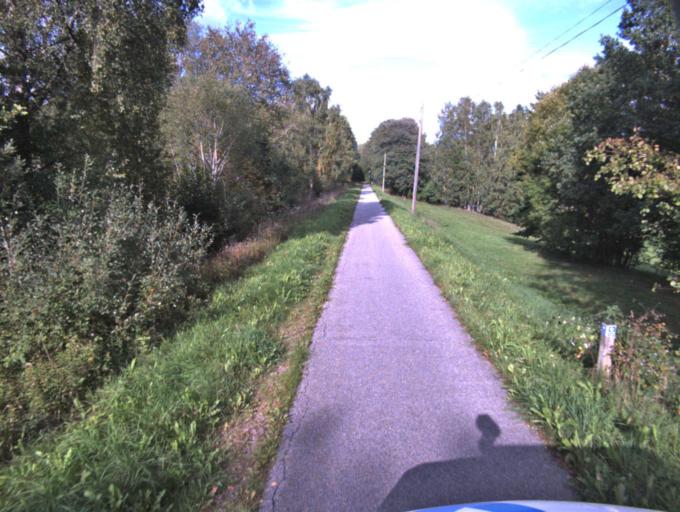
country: SE
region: Vaestra Goetaland
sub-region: Ulricehamns Kommun
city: Ulricehamn
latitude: 57.9031
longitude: 13.4677
